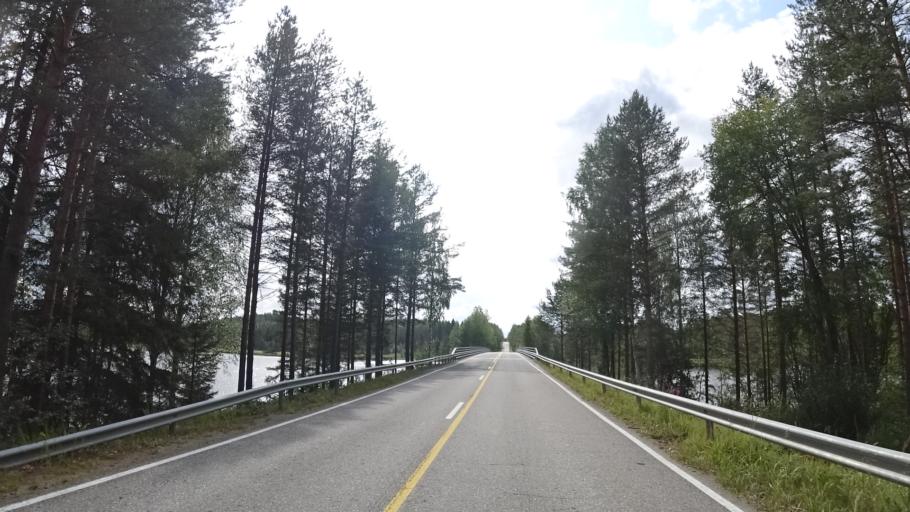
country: FI
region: North Karelia
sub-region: Joensuu
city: Ilomantsi
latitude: 62.7591
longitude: 31.0131
